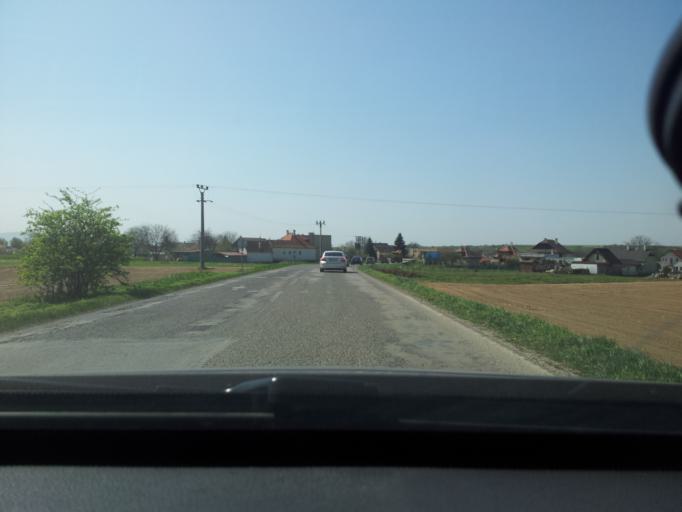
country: SK
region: Nitriansky
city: Banovce nad Bebravou
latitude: 48.6983
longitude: 18.2493
